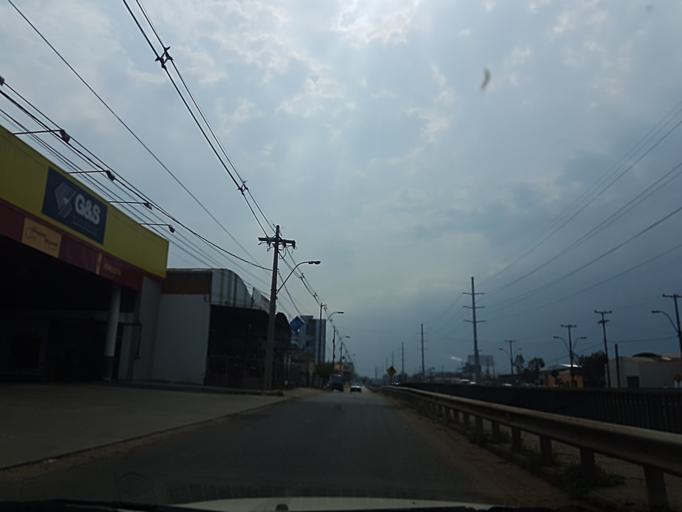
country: PY
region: Central
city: Fernando de la Mora
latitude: -25.2872
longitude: -57.5487
